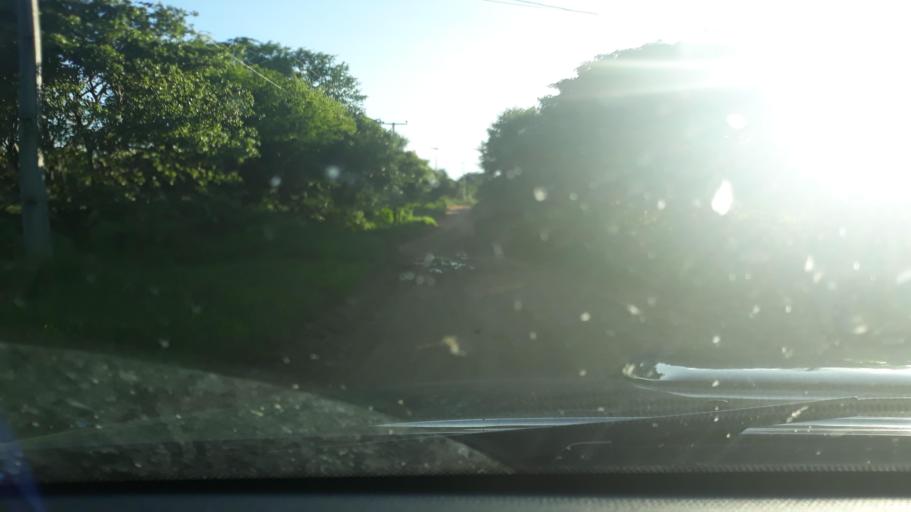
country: BR
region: Bahia
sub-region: Riacho De Santana
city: Riacho de Santana
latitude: -13.8390
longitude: -42.7340
